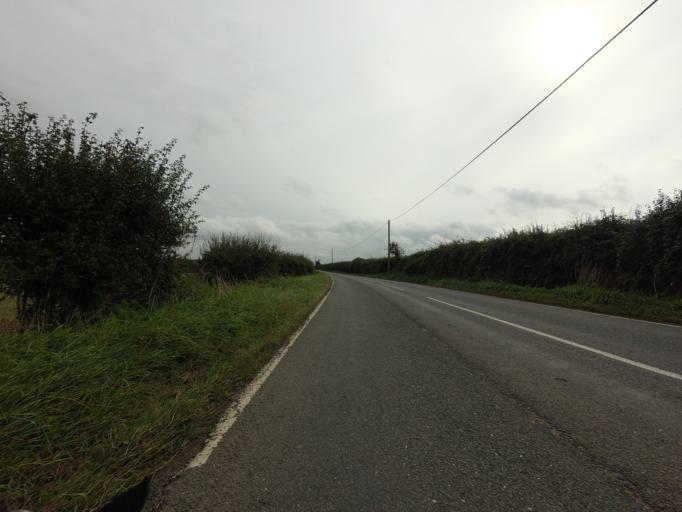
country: GB
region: England
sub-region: Cambridgeshire
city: Duxford
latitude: 52.0177
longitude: 0.1476
